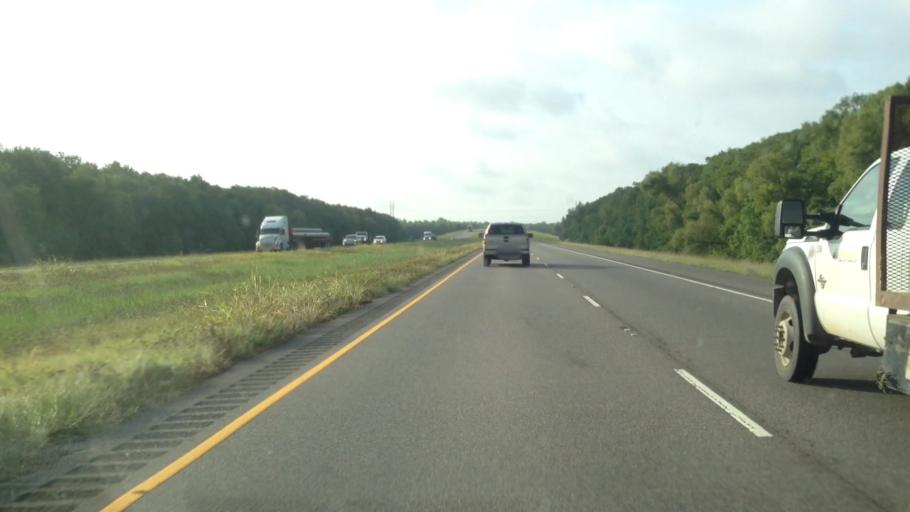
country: US
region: Louisiana
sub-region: Avoyelles Parish
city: Bunkie
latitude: 30.9050
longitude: -92.2343
